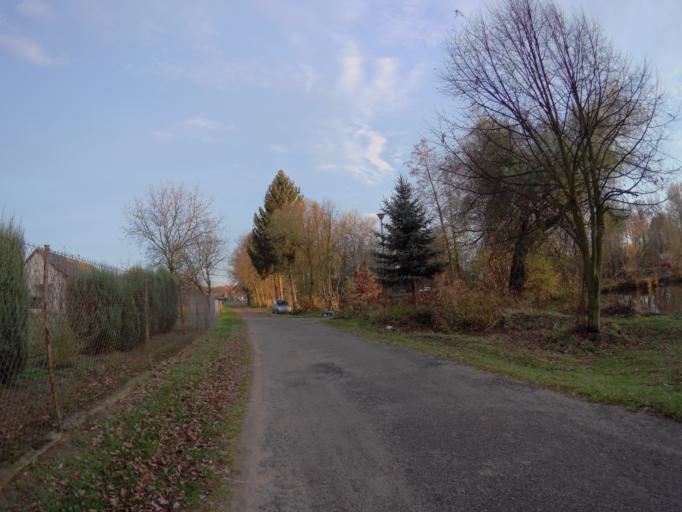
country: PL
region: Subcarpathian Voivodeship
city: Nowa Sarzyna
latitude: 50.3150
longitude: 22.3345
